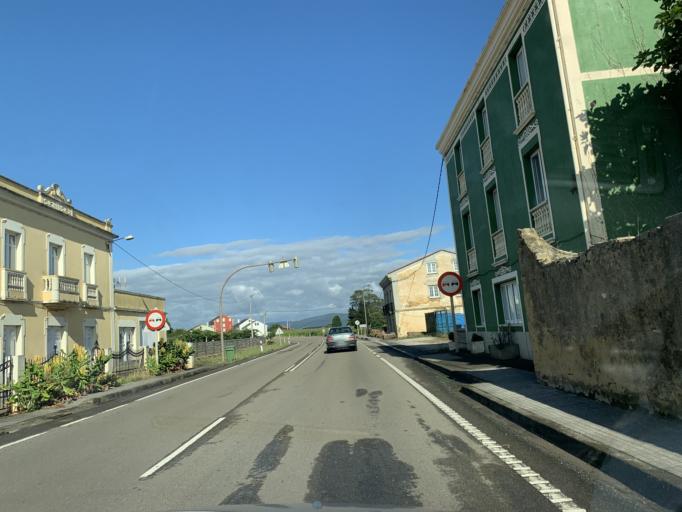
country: ES
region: Galicia
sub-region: Provincia de Lugo
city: Barreiros
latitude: 43.5452
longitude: -7.1960
